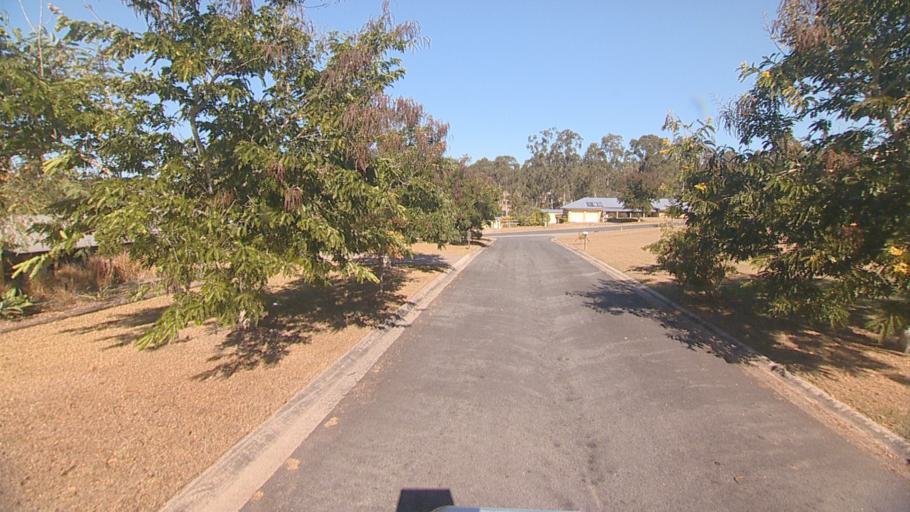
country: AU
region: Queensland
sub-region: Logan
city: Cedar Vale
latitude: -27.8677
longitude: 153.0389
